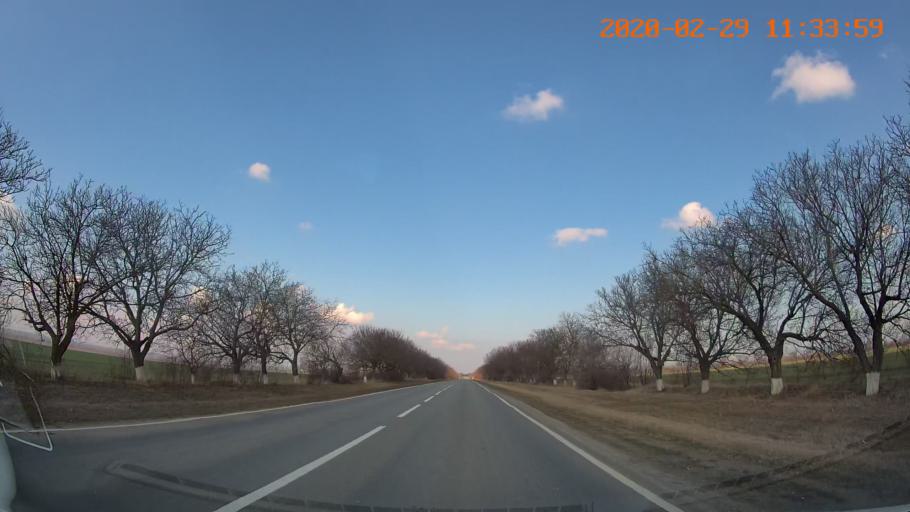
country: MD
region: Rezina
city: Saharna
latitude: 47.5592
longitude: 29.0787
